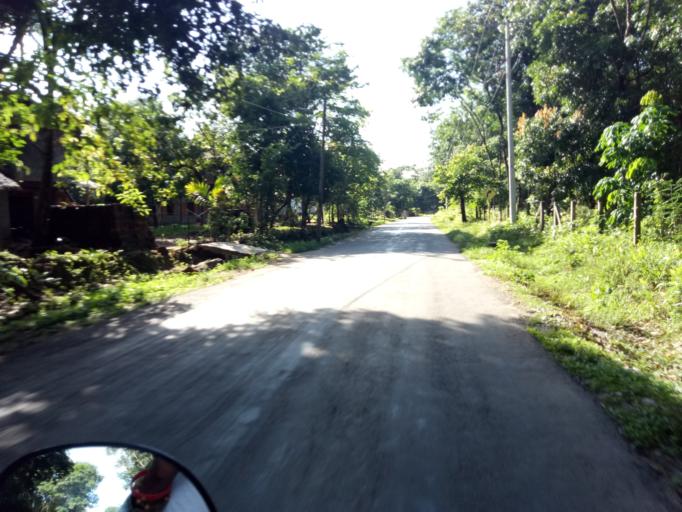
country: MM
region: Mon
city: Mawlamyine
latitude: 16.3799
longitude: 97.5510
